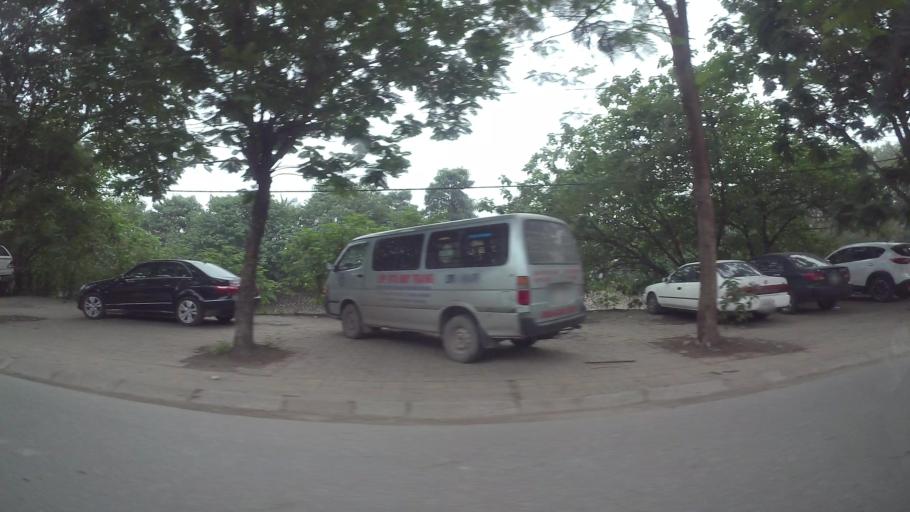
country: VN
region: Ha Noi
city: Hai BaTrung
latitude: 20.9818
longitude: 105.8642
